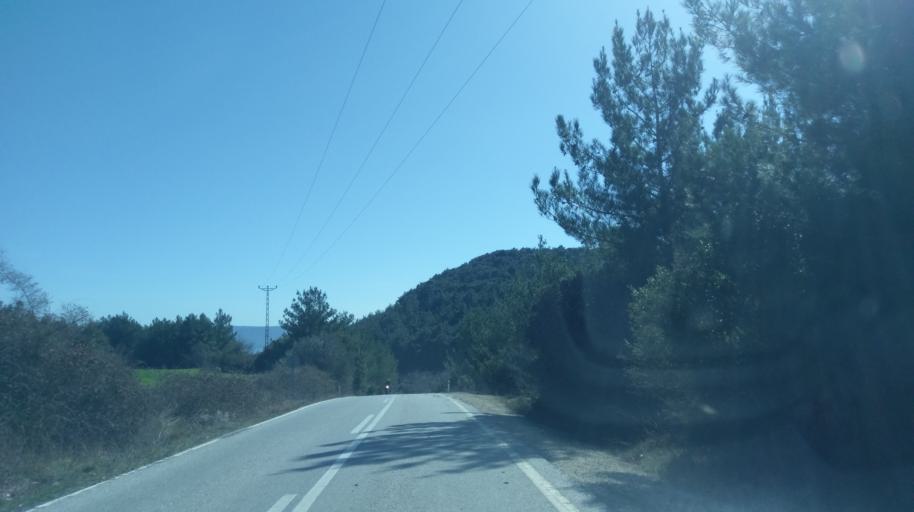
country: TR
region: Canakkale
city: Eceabat
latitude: 40.1202
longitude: 26.2978
